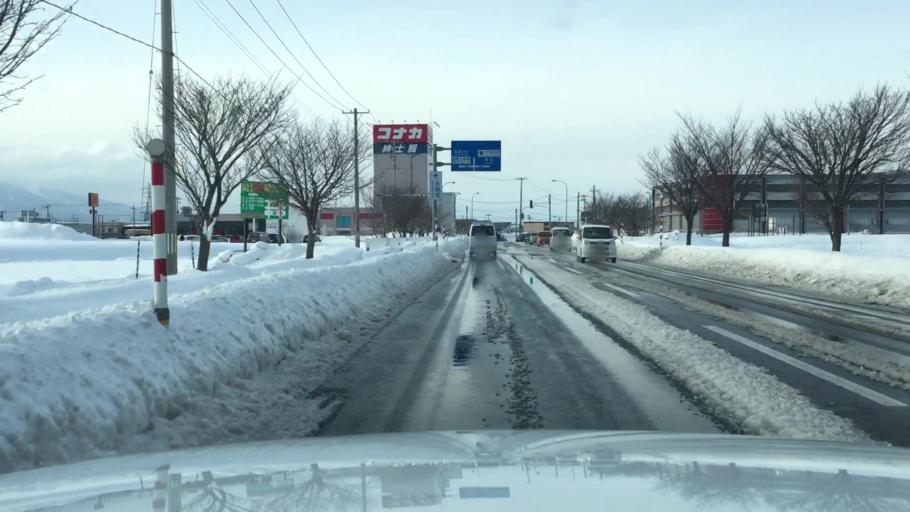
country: JP
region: Aomori
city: Hirosaki
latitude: 40.5978
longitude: 140.5151
